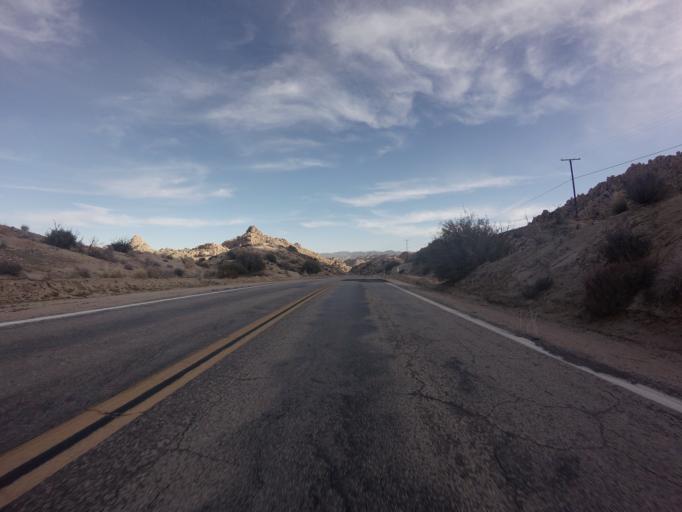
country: US
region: California
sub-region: San Bernardino County
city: Yucca Valley
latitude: 34.1462
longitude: -116.4787
